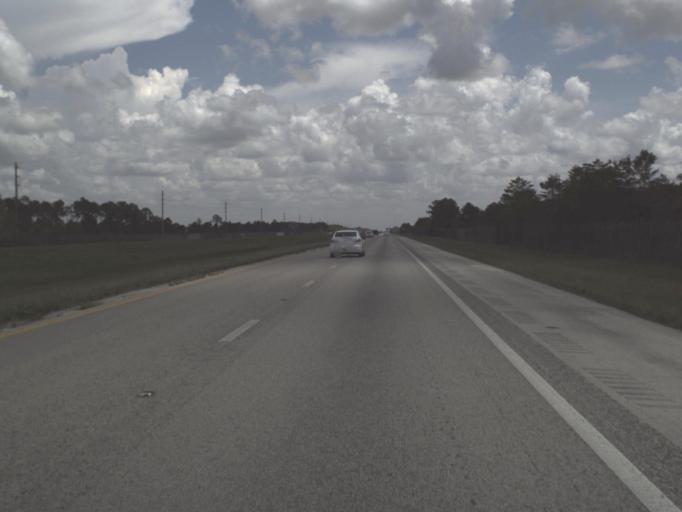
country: US
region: Florida
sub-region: Collier County
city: Immokalee
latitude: 26.1706
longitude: -80.9694
